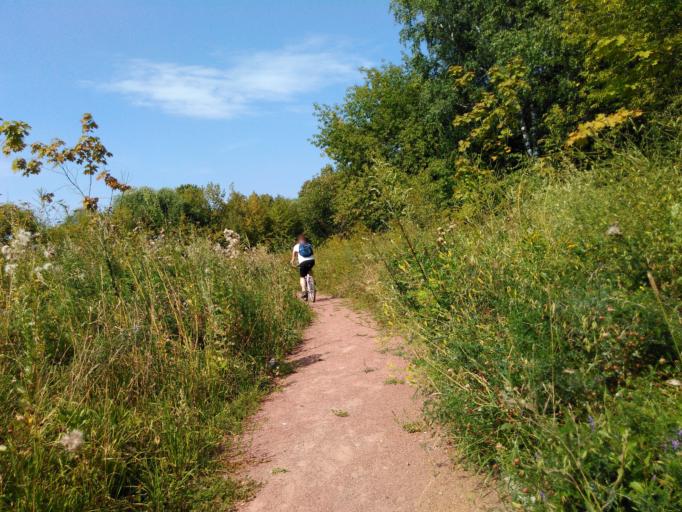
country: RU
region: Moskovskaya
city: Bol'shaya Setun'
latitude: 55.7099
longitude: 37.4152
